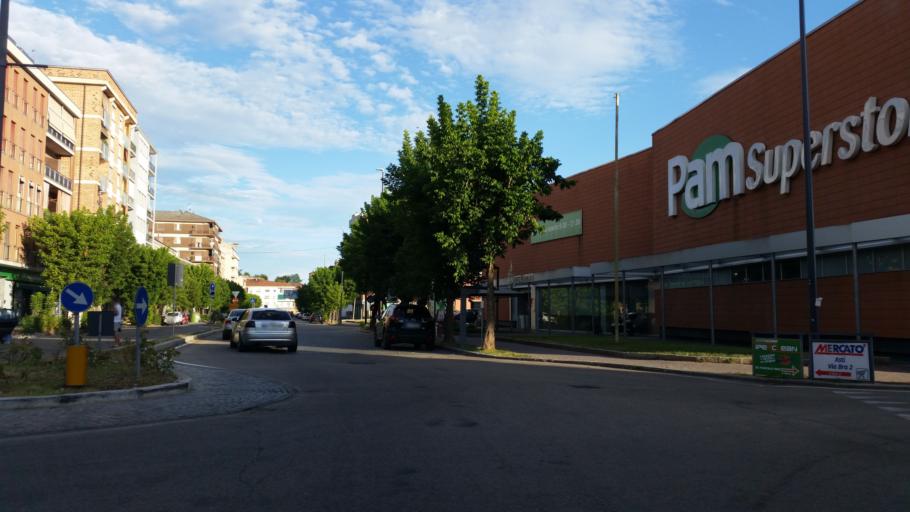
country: IT
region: Piedmont
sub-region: Provincia di Asti
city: Asti
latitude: 44.9023
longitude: 8.1908
